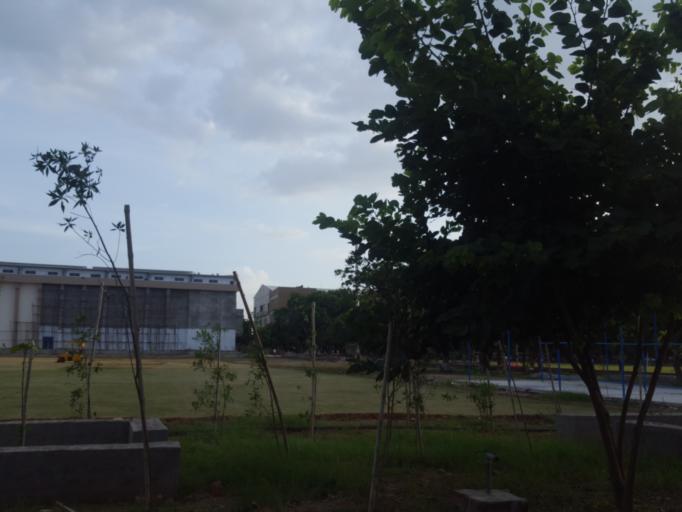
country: IN
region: Telangana
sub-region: Rangareddi
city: Quthbullapur
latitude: 17.5958
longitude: 78.4428
